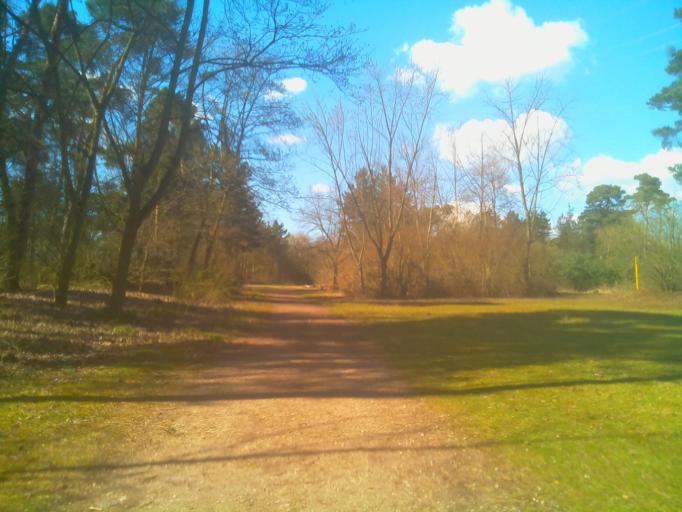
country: DE
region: Baden-Wuerttemberg
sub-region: Karlsruhe Region
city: Ilvesheim
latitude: 49.4473
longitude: 8.5360
